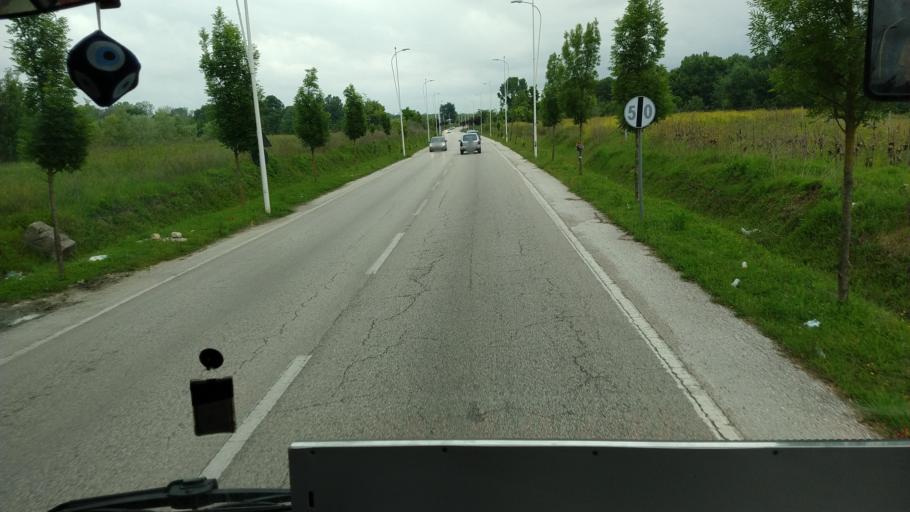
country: AL
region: Tirane
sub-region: Rrethi i Tiranes
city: Berxull
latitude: 41.4104
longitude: 19.7035
